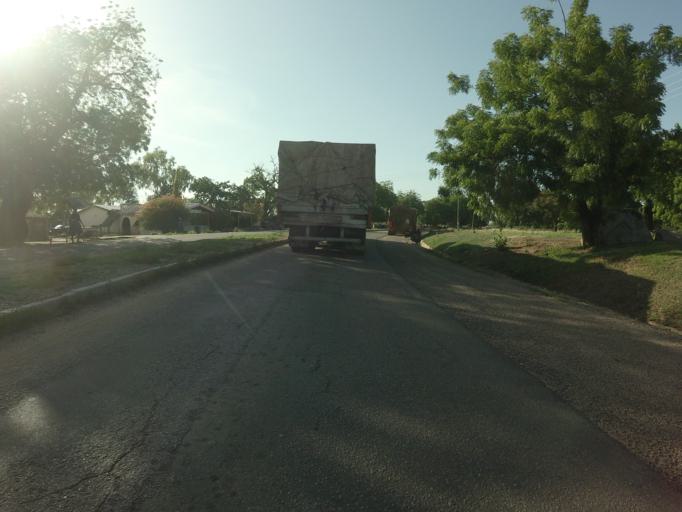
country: GH
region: Upper East
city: Navrongo
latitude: 10.8986
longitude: -1.0924
